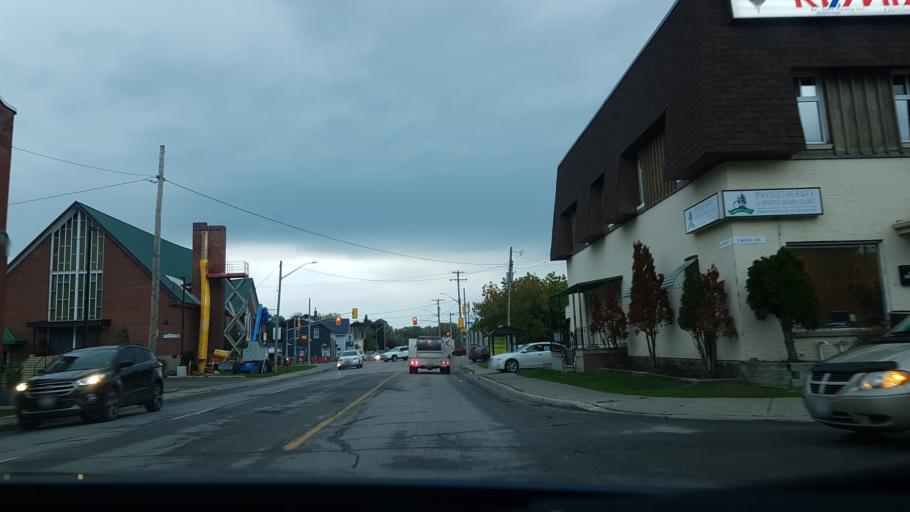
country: CA
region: Ontario
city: Omemee
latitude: 44.3571
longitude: -78.7355
